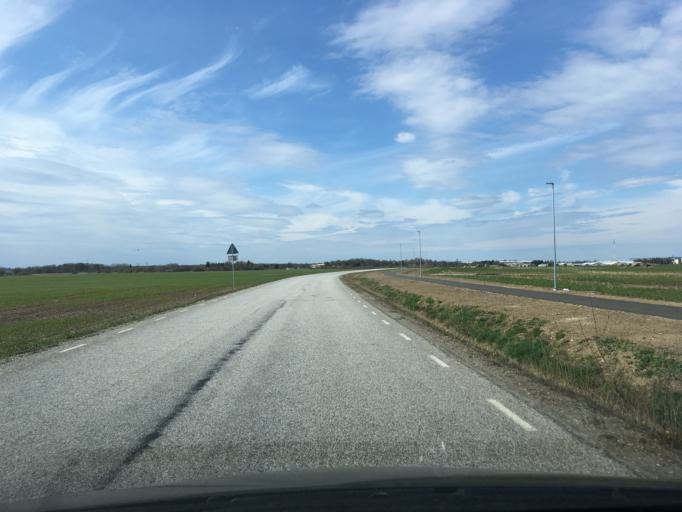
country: EE
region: Harju
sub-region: Raasiku vald
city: Arukula
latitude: 59.4157
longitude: 25.1144
